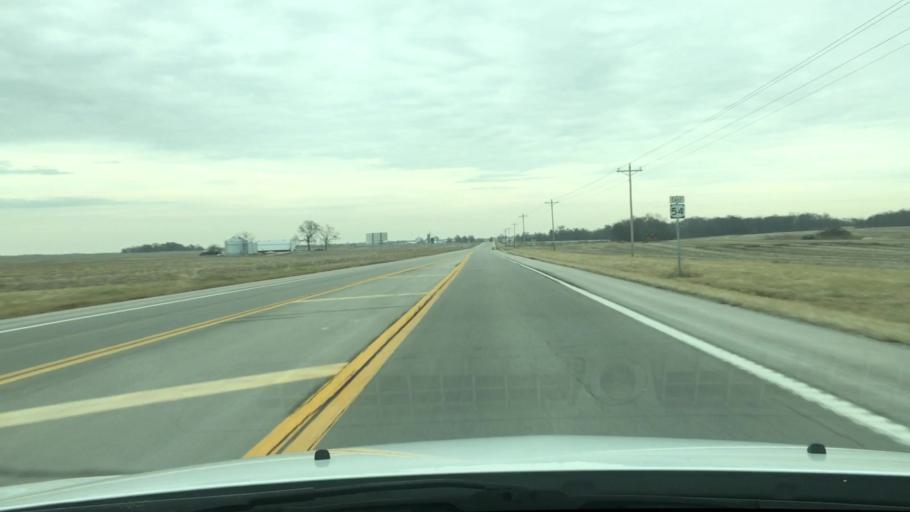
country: US
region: Missouri
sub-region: Audrain County
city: Mexico
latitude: 39.1642
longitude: -91.7231
